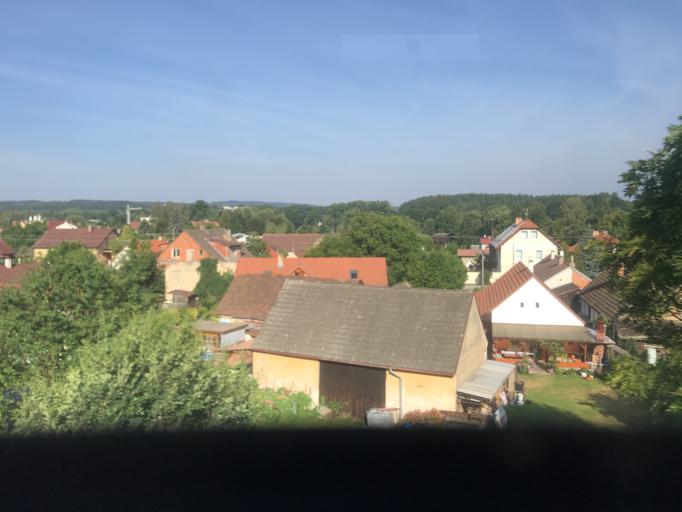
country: CZ
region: Jihocesky
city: Sobeslav
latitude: 49.3043
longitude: 14.7200
